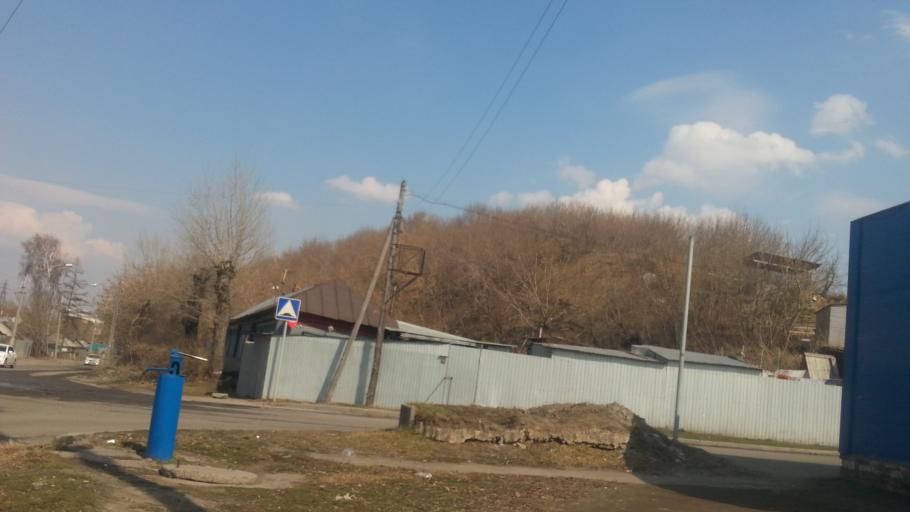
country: RU
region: Altai Krai
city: Zaton
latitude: 53.3205
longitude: 83.7799
